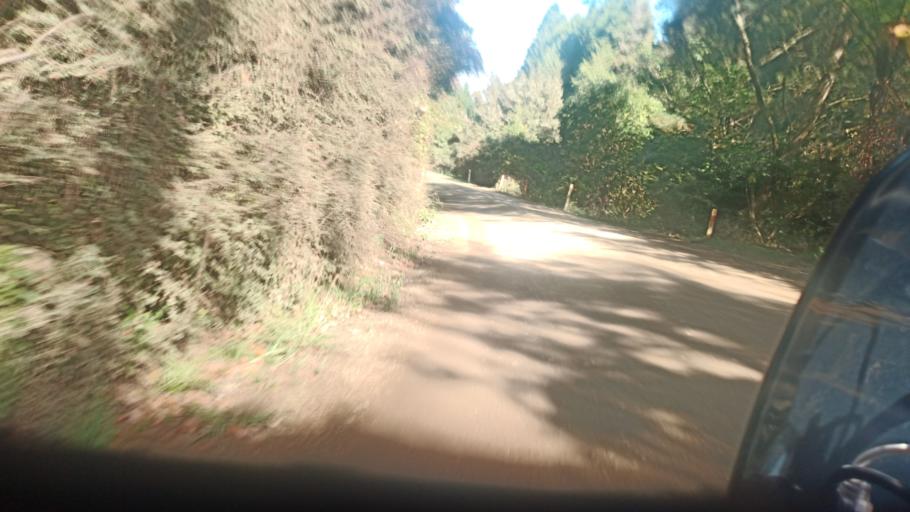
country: NZ
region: Bay of Plenty
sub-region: Opotiki District
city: Opotiki
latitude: -38.4173
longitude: 177.5596
